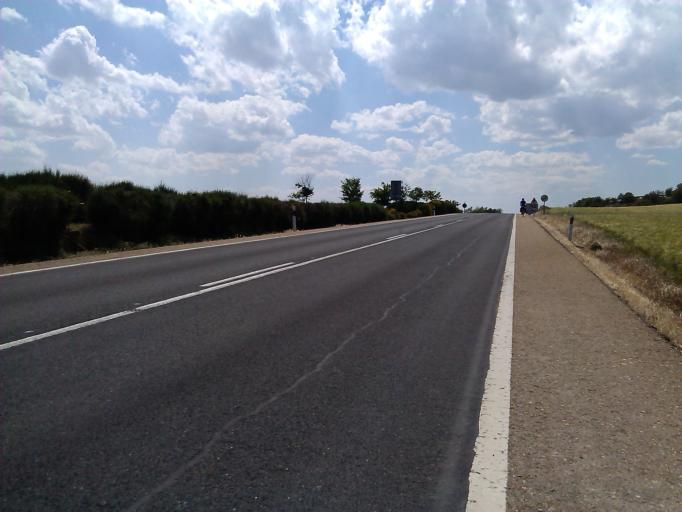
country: ES
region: Castille and Leon
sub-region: Provincia de Palencia
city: Moratinos
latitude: 42.3626
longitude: -4.9235
